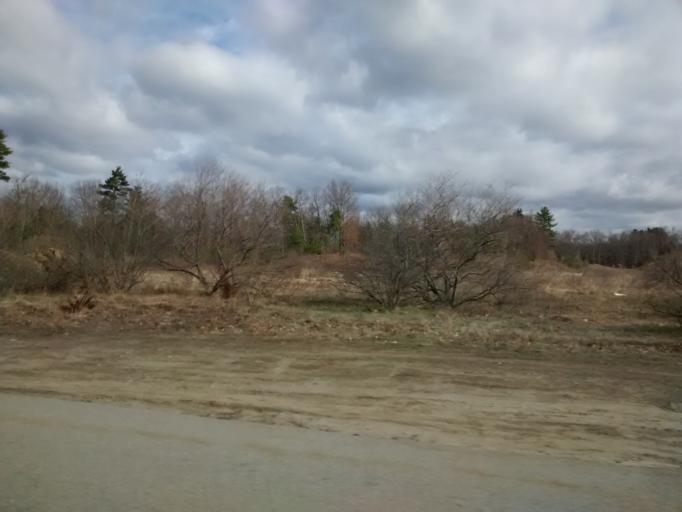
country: US
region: Massachusetts
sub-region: Worcester County
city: East Douglas
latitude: 42.1018
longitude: -71.6997
